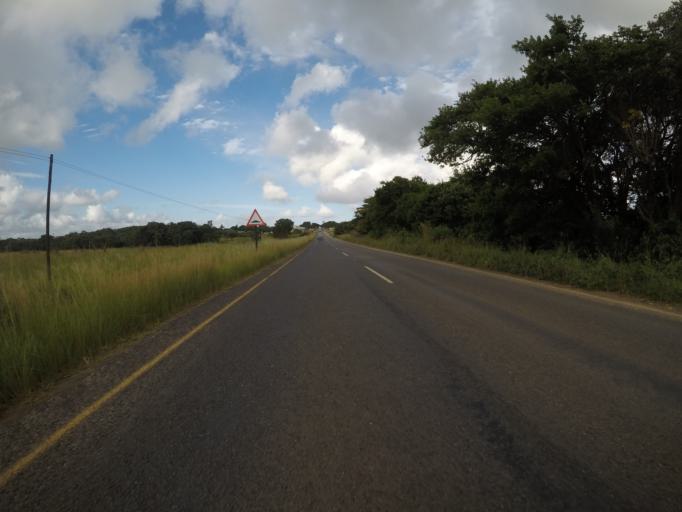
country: ZA
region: KwaZulu-Natal
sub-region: uMkhanyakude District Municipality
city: Mtubatuba
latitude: -28.3859
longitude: 32.3468
